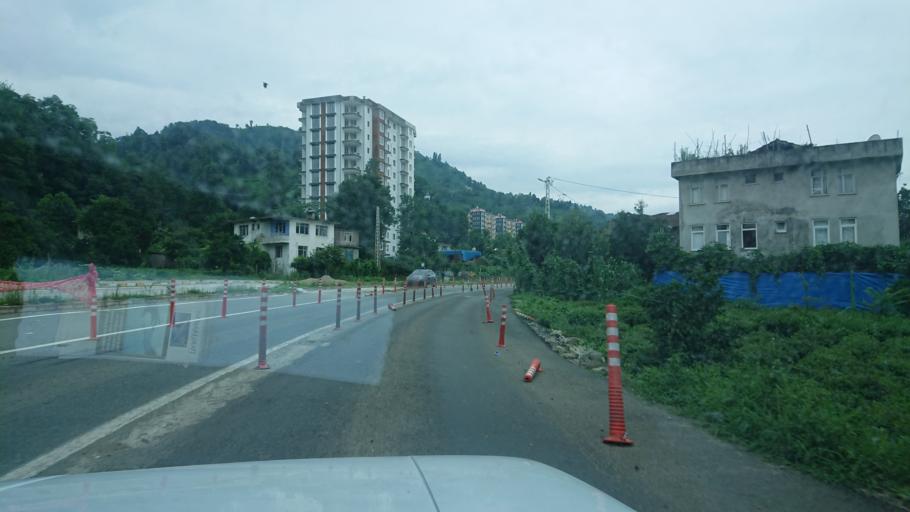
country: TR
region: Rize
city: Gundogdu
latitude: 41.0371
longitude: 40.5663
